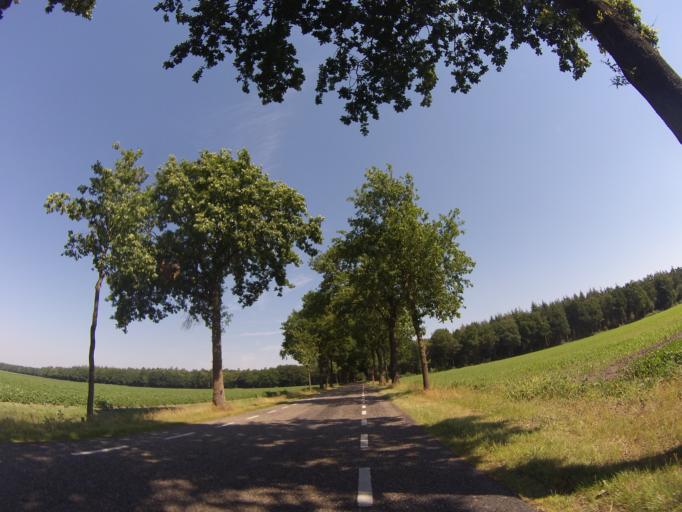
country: NL
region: Drenthe
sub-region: Gemeente Coevorden
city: Sleen
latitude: 52.8183
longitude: 6.7428
